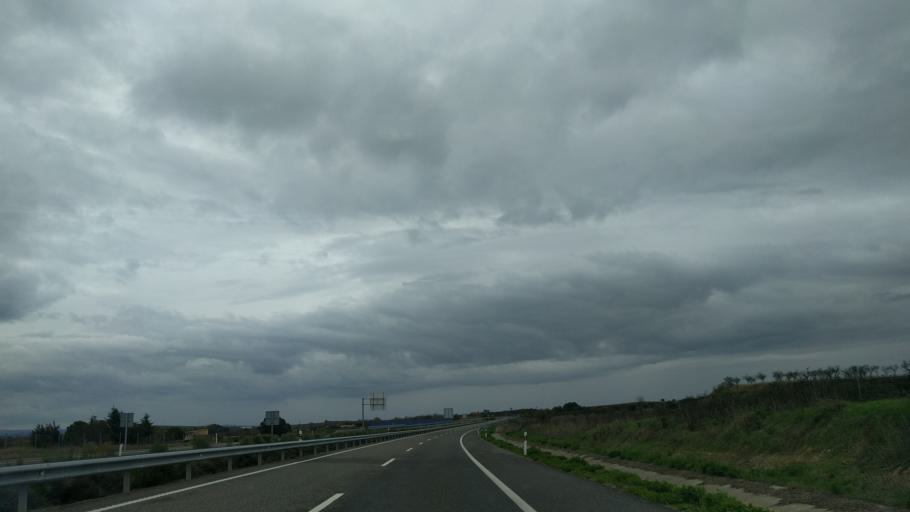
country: ES
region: Aragon
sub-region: Provincia de Huesca
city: Barbastro
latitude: 41.9964
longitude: 0.1033
